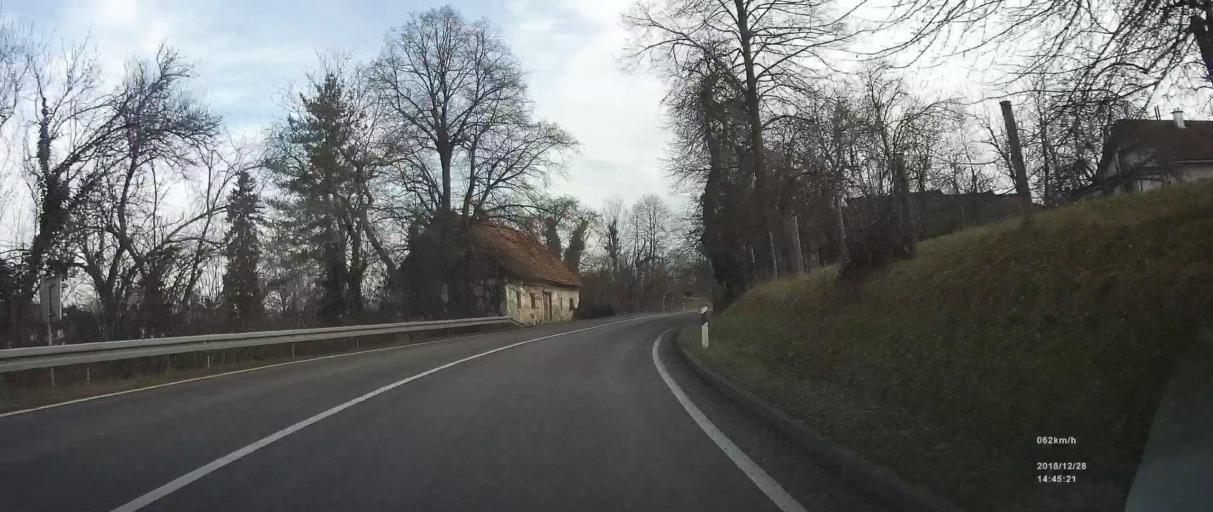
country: SI
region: Crnomelj
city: Crnomelj
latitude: 45.4526
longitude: 15.3034
